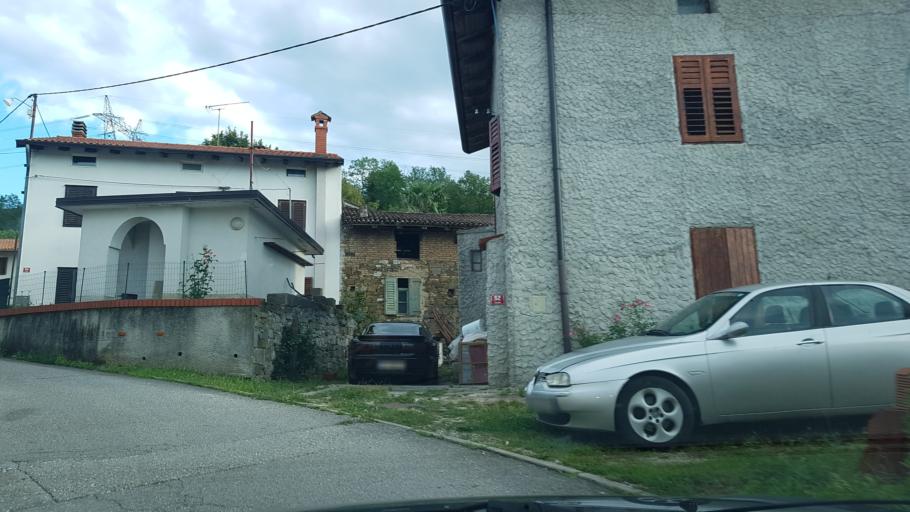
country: SI
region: Rence-Vogrsko
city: Rence
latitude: 45.8799
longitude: 13.6653
